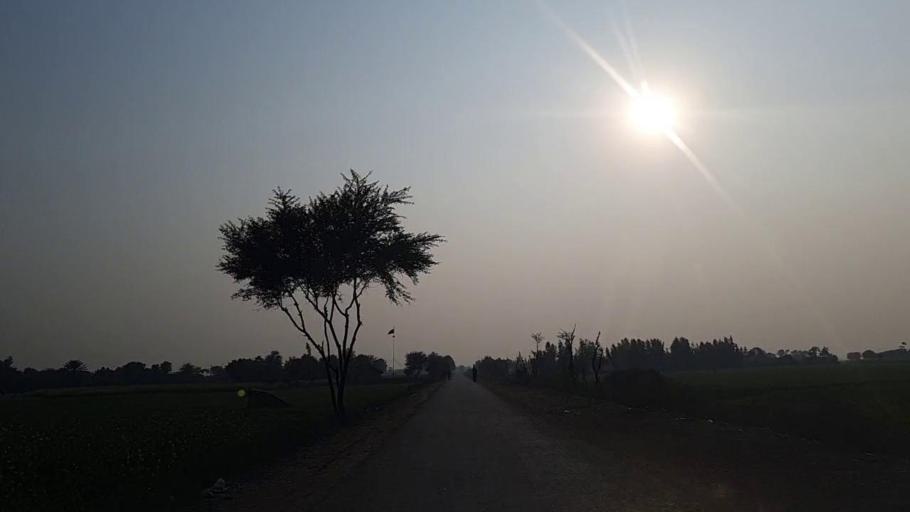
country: PK
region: Sindh
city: Nawabshah
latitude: 26.2240
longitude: 68.4787
